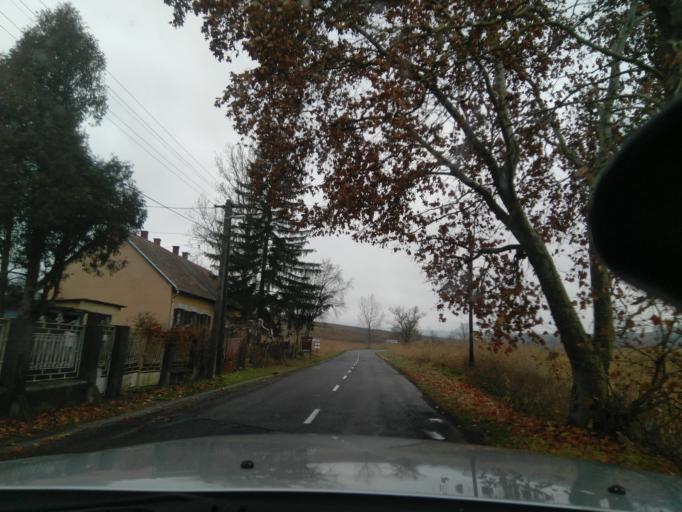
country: HU
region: Nograd
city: Kazar
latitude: 48.0325
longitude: 19.8725
